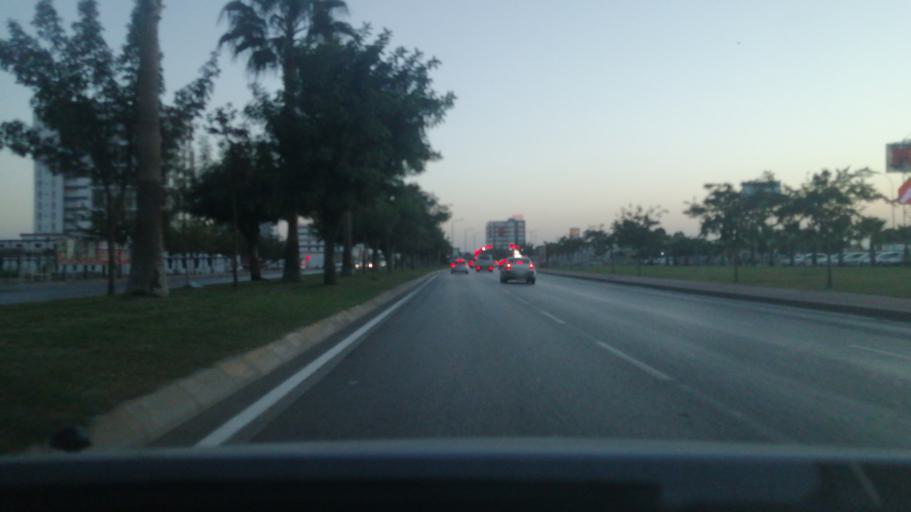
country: TR
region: Adana
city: Seyhan
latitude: 37.0179
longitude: 35.2517
